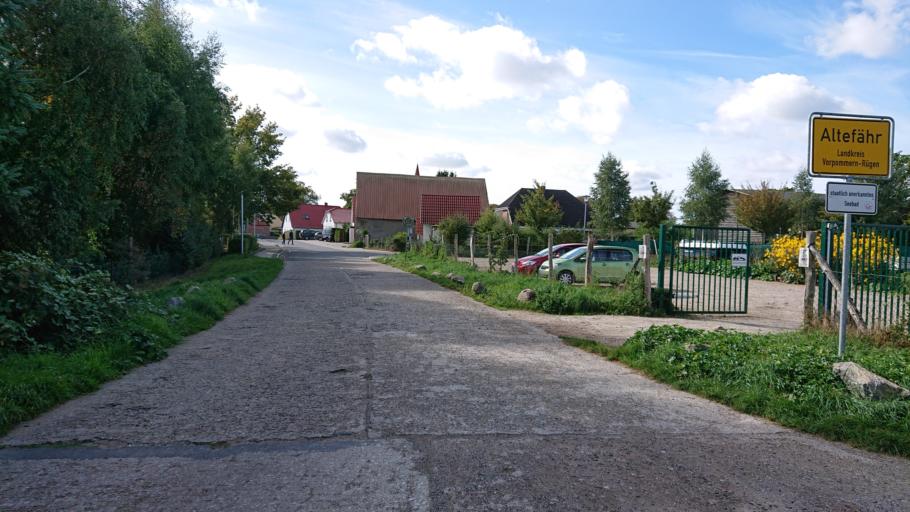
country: DE
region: Mecklenburg-Vorpommern
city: Altefahr
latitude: 54.3321
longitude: 13.1269
